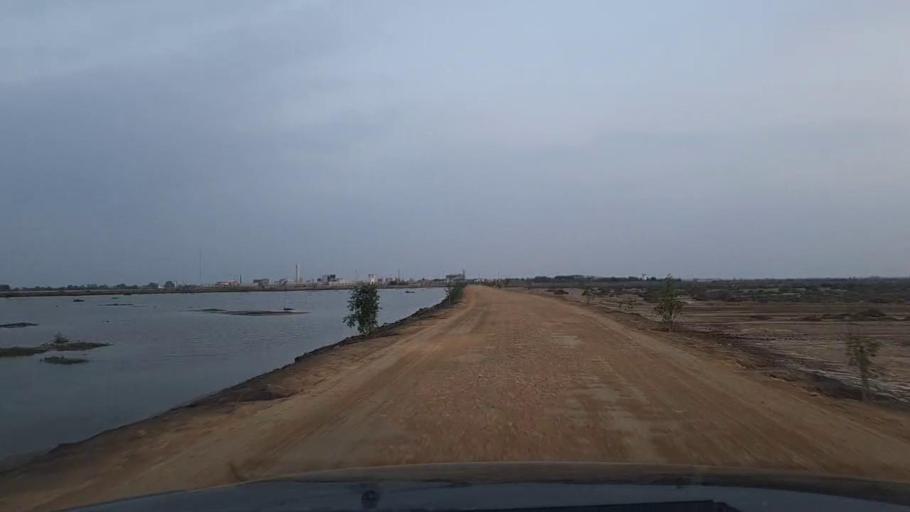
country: PK
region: Sindh
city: Jati
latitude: 24.4935
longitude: 68.3886
